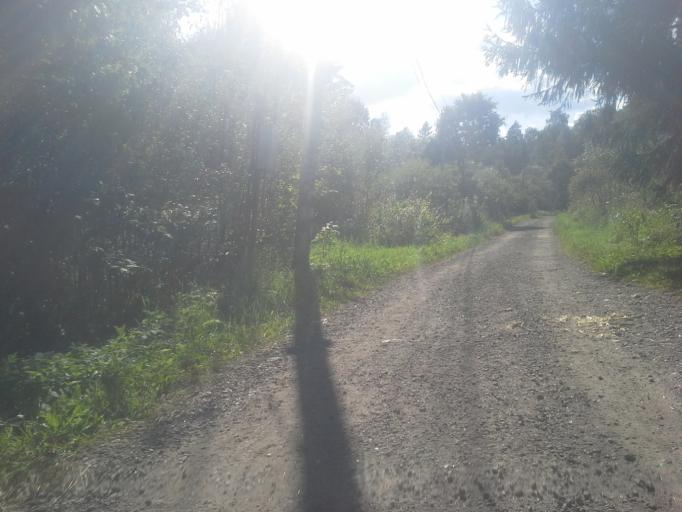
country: RU
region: Moskovskaya
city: Kievskij
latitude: 55.3412
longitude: 36.9725
